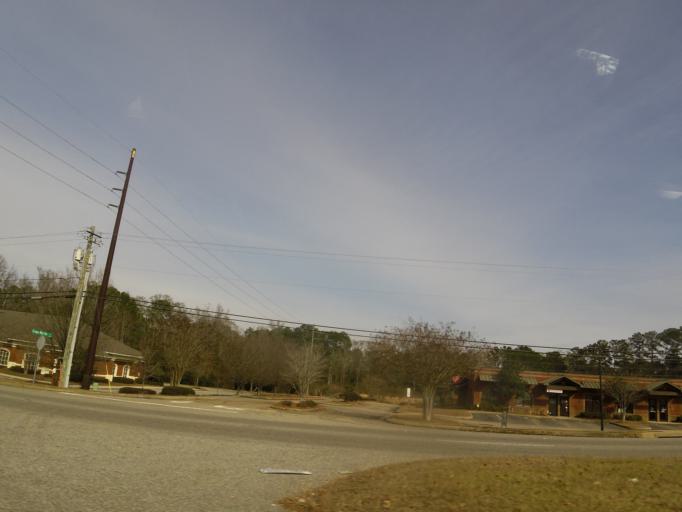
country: US
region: Alabama
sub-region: Houston County
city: Dothan
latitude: 31.2449
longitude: -85.4203
